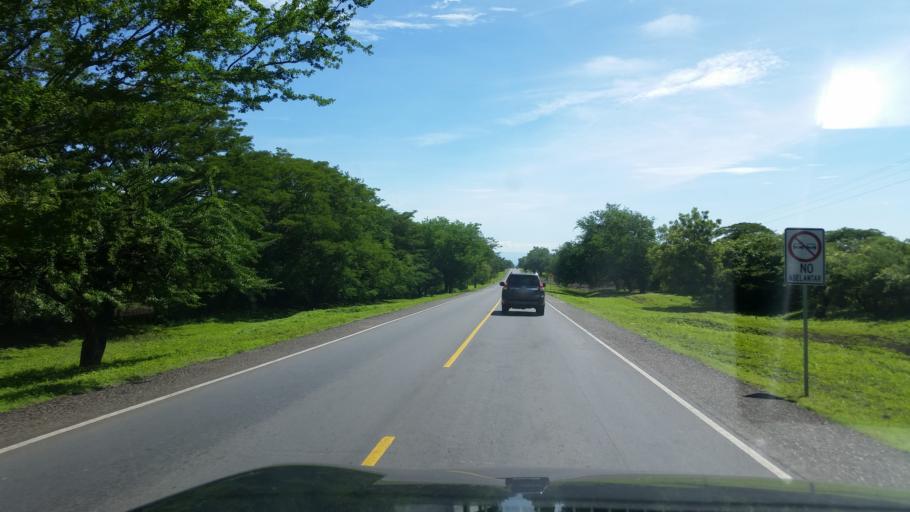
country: NI
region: Chinandega
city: El Viejo
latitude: 12.7455
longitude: -87.0708
